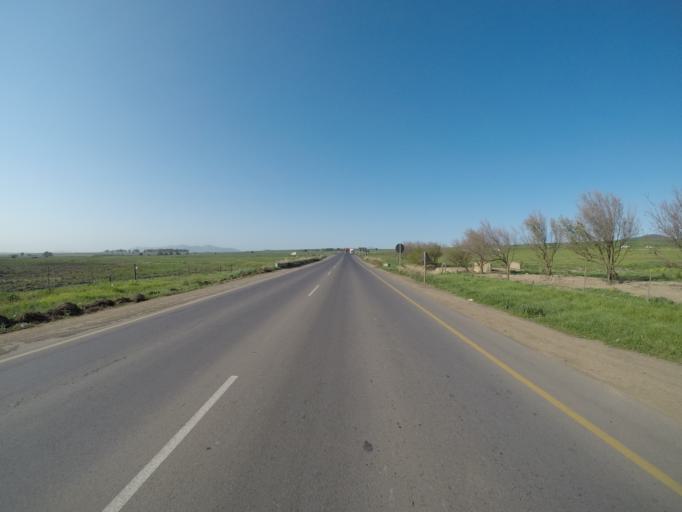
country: ZA
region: Western Cape
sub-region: City of Cape Town
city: Kraaifontein
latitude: -33.7705
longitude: 18.7549
